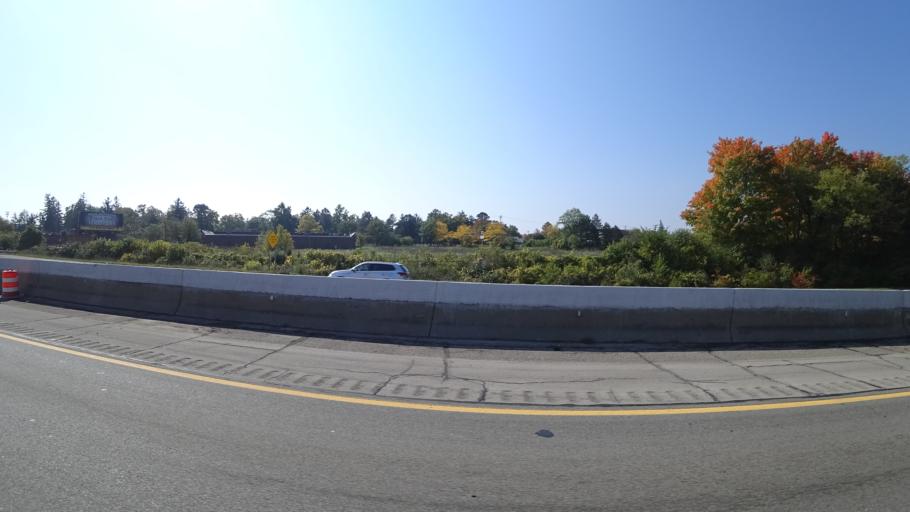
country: US
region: Michigan
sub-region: Washtenaw County
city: Ann Arbor
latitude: 42.2836
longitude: -83.7854
